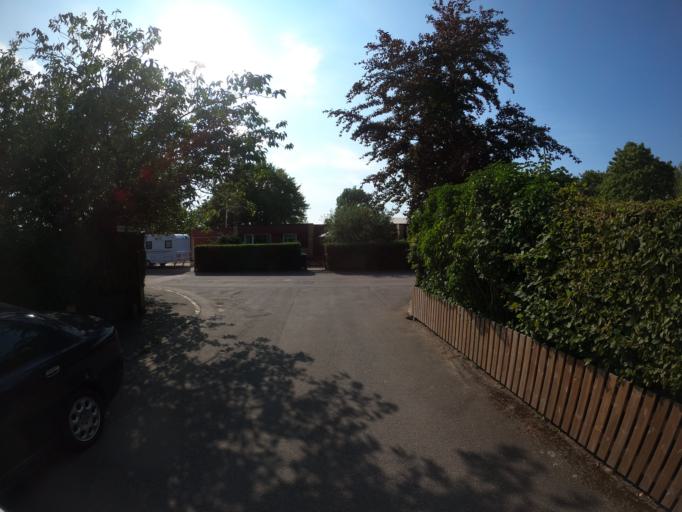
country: SE
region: Skane
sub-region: Lunds Kommun
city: Lund
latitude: 55.7407
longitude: 13.1759
